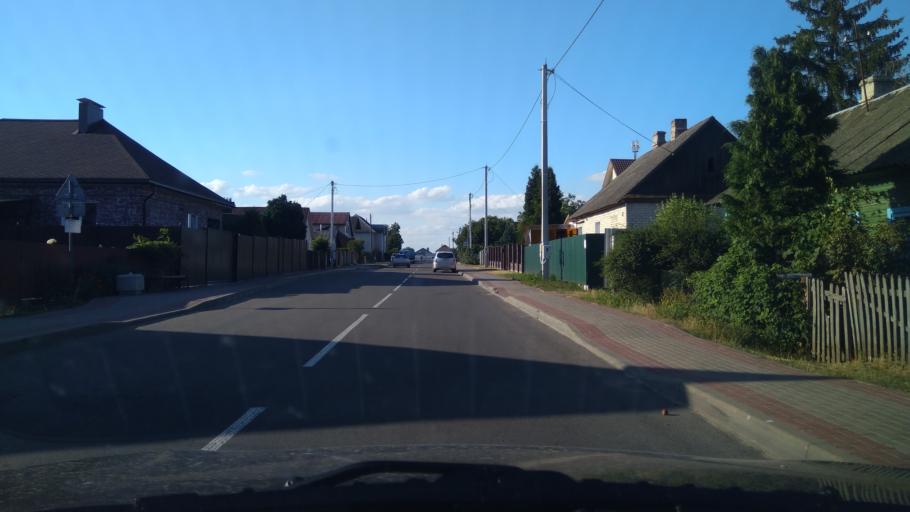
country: BY
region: Brest
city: Byaroza
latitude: 52.5384
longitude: 24.9782
